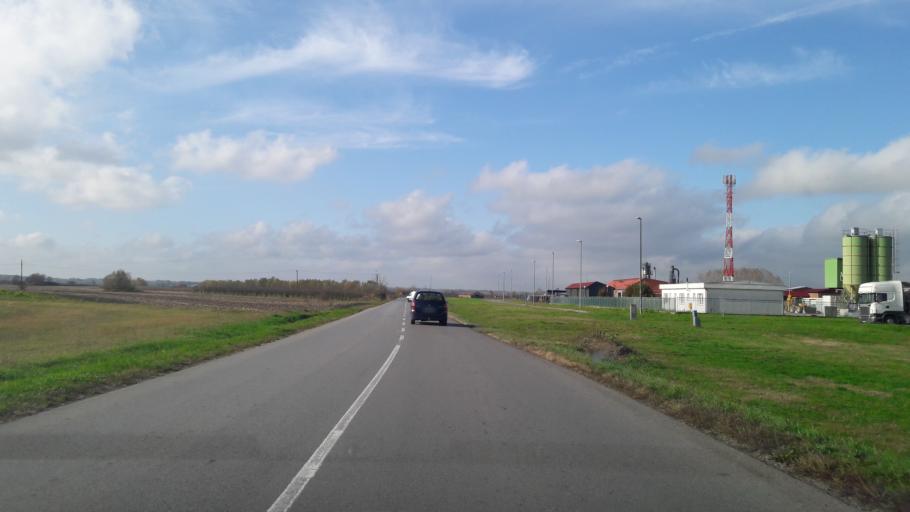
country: HR
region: Osjecko-Baranjska
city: Darda
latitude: 45.6202
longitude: 18.6845
